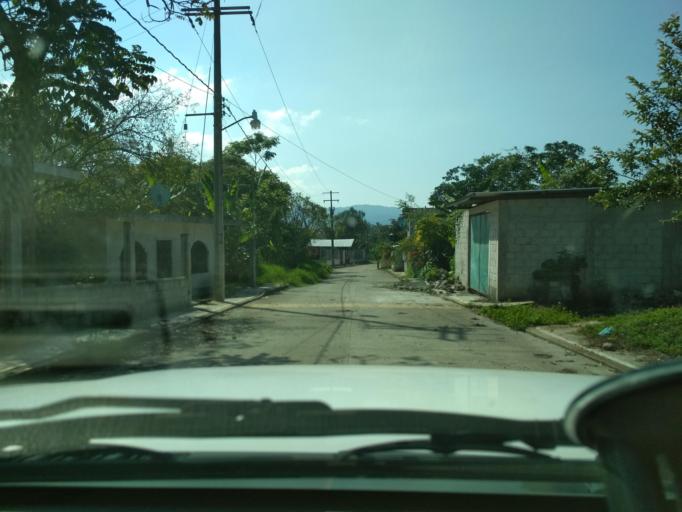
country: MX
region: Veracruz
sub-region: Chocaman
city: San Jose Neria
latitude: 18.9958
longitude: -97.0009
